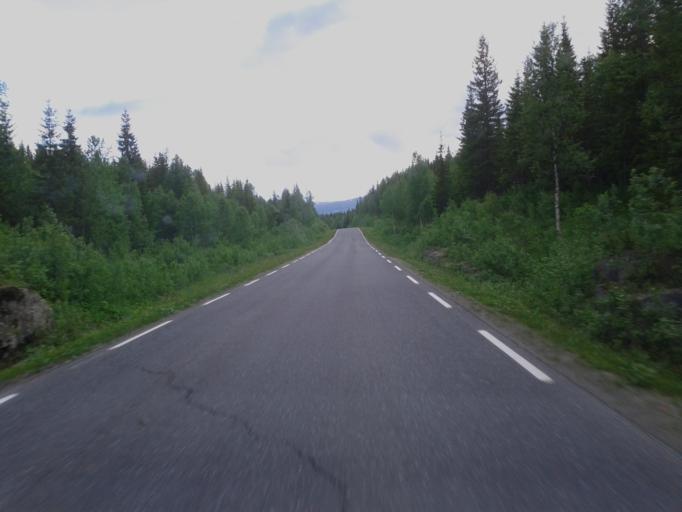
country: NO
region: Nordland
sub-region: Hattfjelldal
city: Hattfjelldal
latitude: 65.5507
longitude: 13.7299
